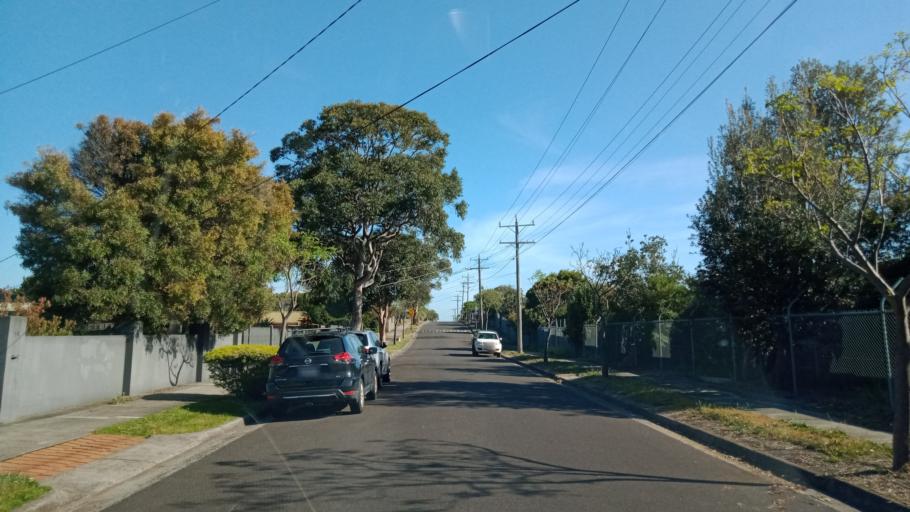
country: AU
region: Victoria
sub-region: Kingston
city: Chelsea Heights
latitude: -38.0432
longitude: 145.1372
